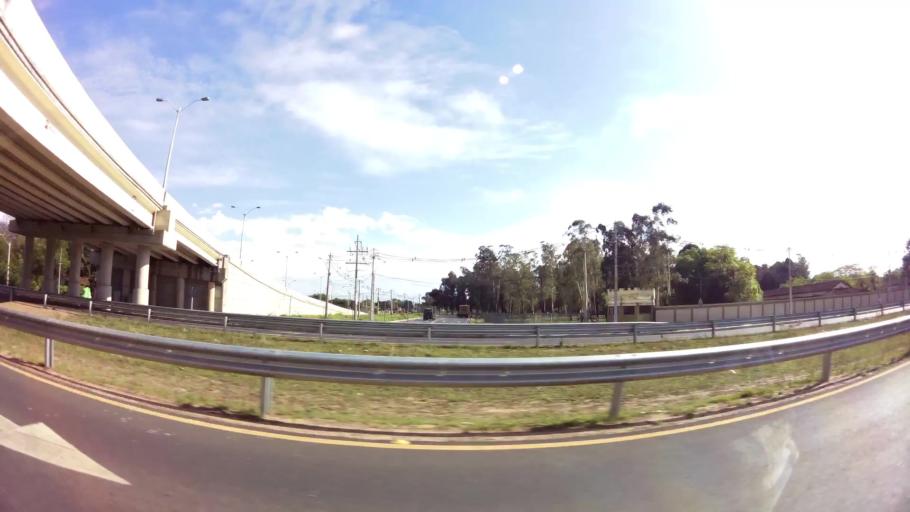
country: PY
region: Central
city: Fernando de la Mora
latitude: -25.2568
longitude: -57.5507
